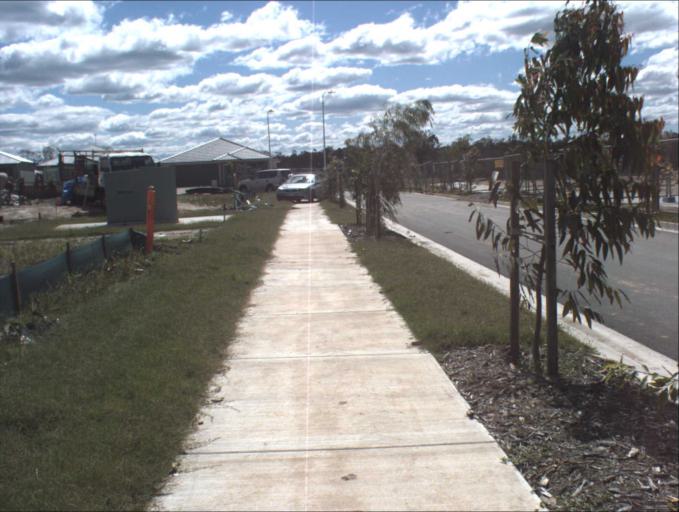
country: AU
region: Queensland
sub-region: Logan
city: Chambers Flat
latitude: -27.8011
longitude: 153.1157
